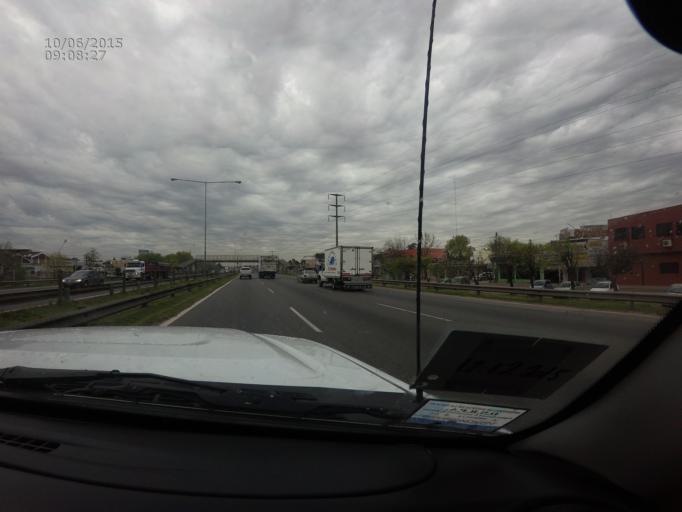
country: AR
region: Buenos Aires
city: Santa Catalina - Dique Lujan
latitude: -34.3897
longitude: -58.7443
